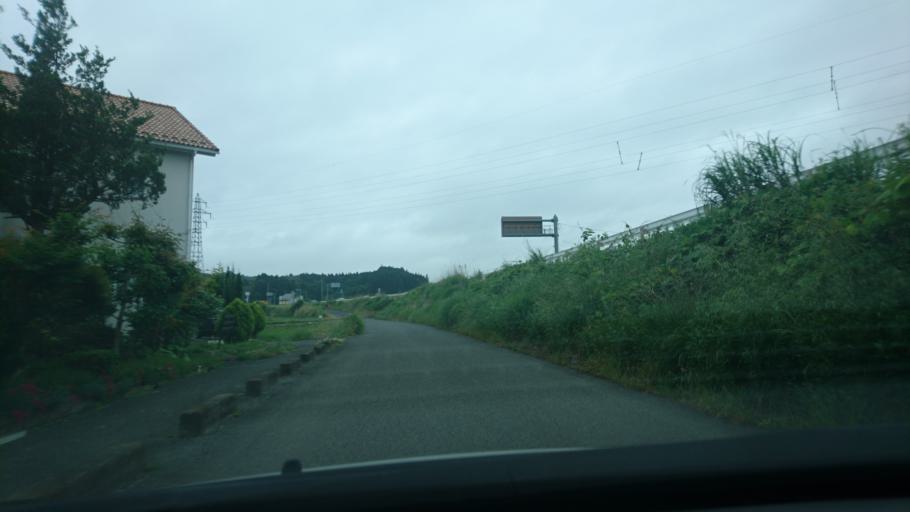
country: JP
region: Iwate
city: Ichinoseki
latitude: 38.9178
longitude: 141.1082
